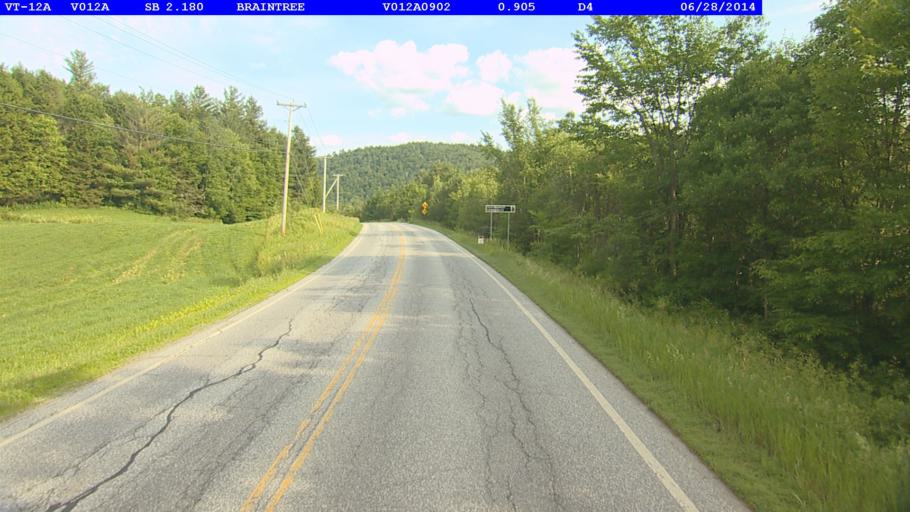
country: US
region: Vermont
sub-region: Orange County
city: Randolph
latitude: 43.9356
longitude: -72.7035
